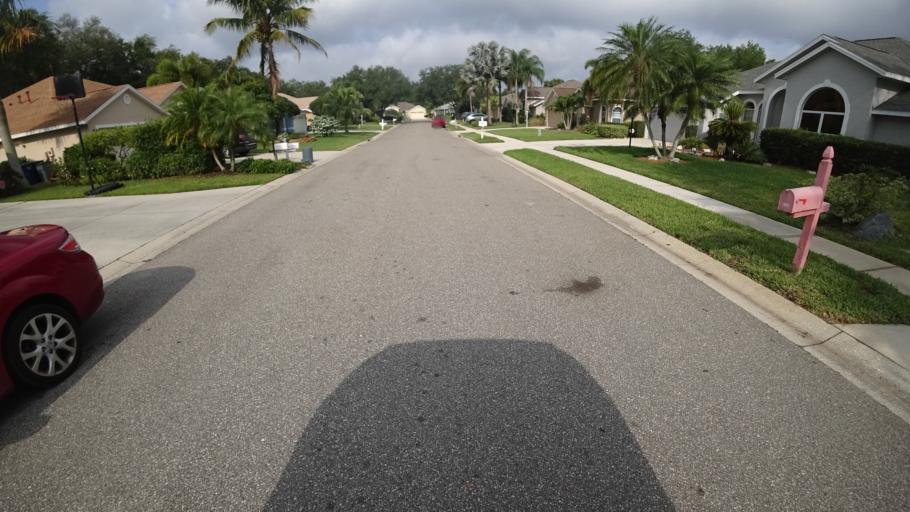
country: US
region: Florida
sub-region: Sarasota County
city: North Sarasota
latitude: 27.4075
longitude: -82.5081
